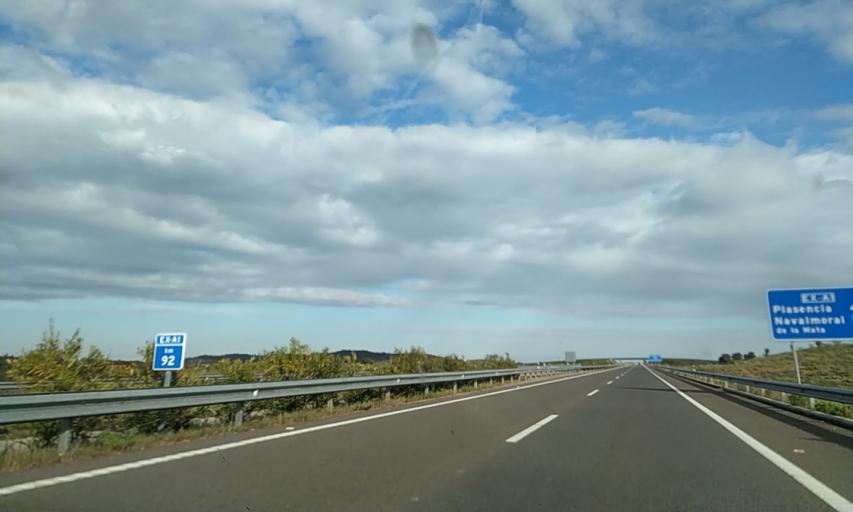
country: ES
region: Extremadura
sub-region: Provincia de Caceres
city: Casas de Don Gomez
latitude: 40.0220
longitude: -6.5972
